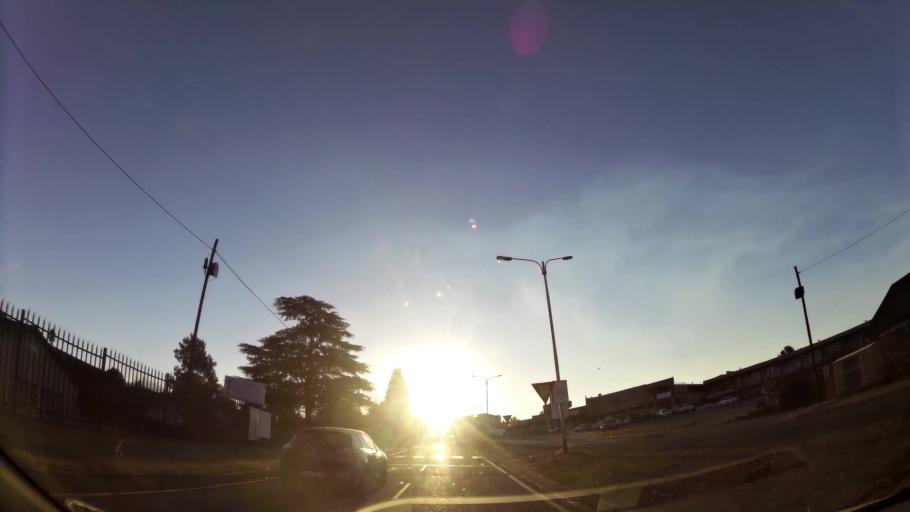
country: ZA
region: Gauteng
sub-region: City of Johannesburg Metropolitan Municipality
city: Roodepoort
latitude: -26.1573
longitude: 27.8863
